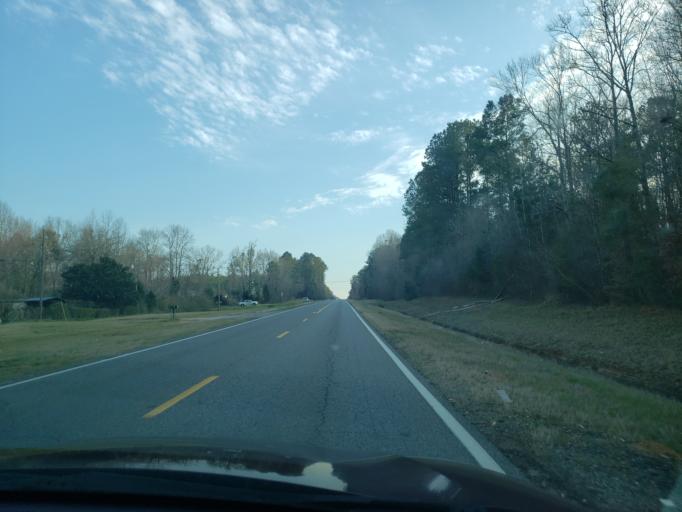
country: US
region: Alabama
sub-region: Hale County
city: Greensboro
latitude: 32.7591
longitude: -87.5853
